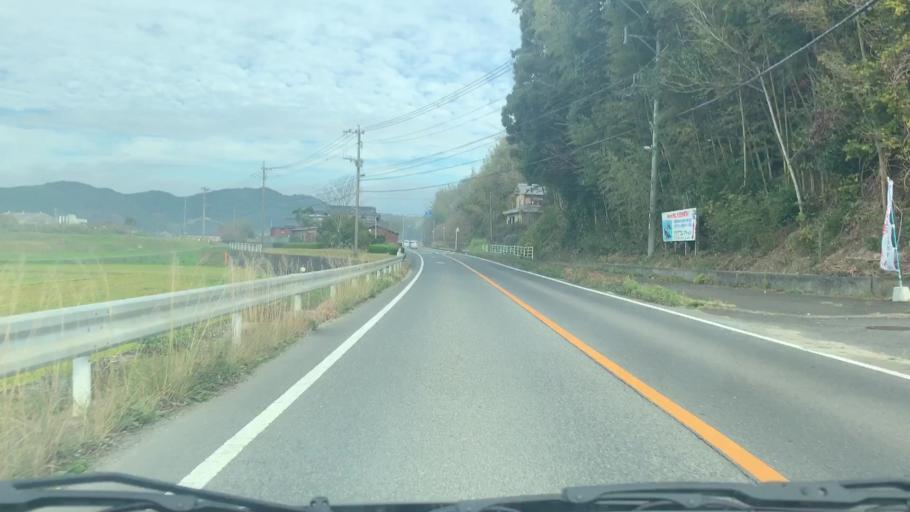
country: JP
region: Saga Prefecture
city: Karatsu
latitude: 33.3908
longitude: 129.9874
